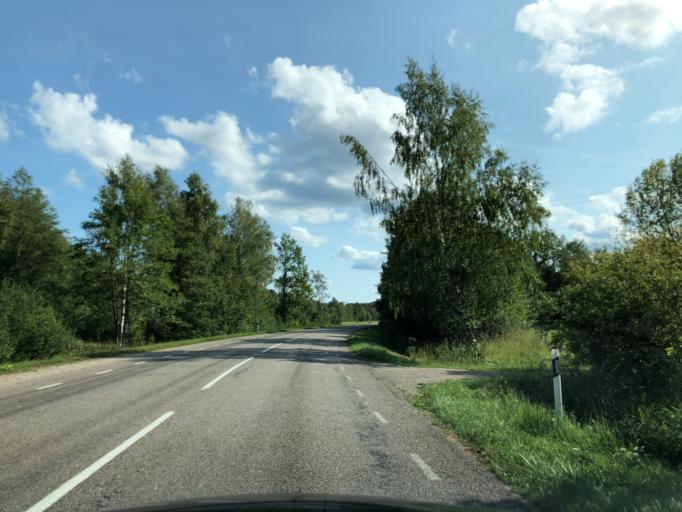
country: EE
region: Hiiumaa
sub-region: Kaerdla linn
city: Kardla
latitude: 58.7241
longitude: 22.5614
